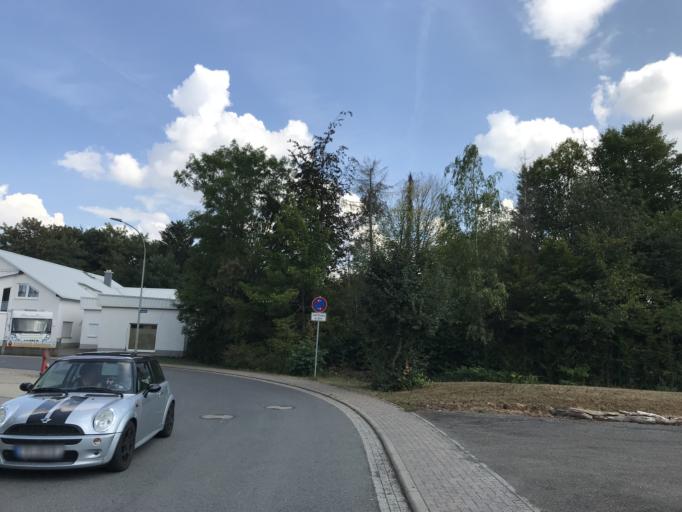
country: DE
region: Hesse
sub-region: Regierungsbezirk Darmstadt
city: Wolfersheim
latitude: 50.3969
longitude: 8.8182
